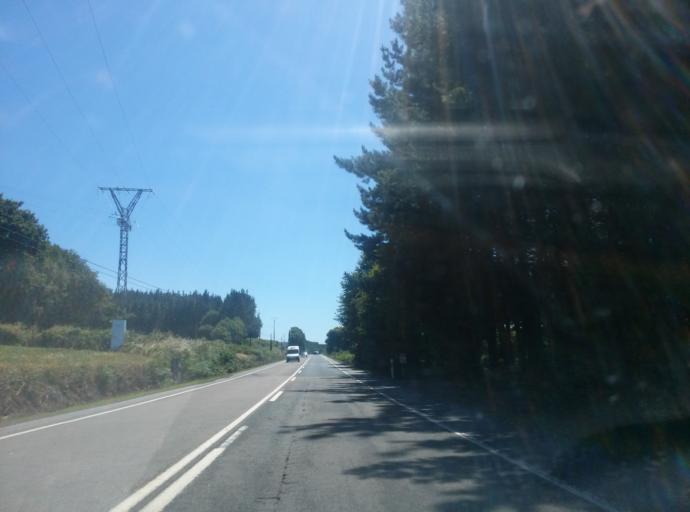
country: ES
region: Galicia
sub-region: Provincia de Lugo
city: Castro de Rei
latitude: 43.1244
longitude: -7.4240
